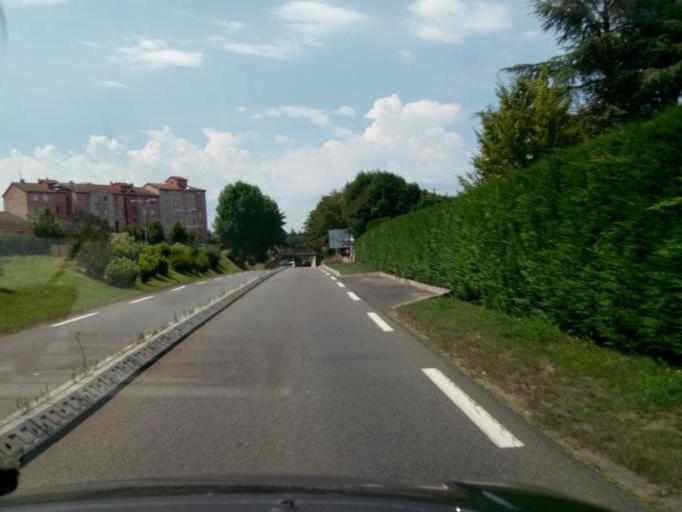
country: FR
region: Rhone-Alpes
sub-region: Departement de la Loire
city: Roche-la-Moliere
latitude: 45.4326
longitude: 4.3249
